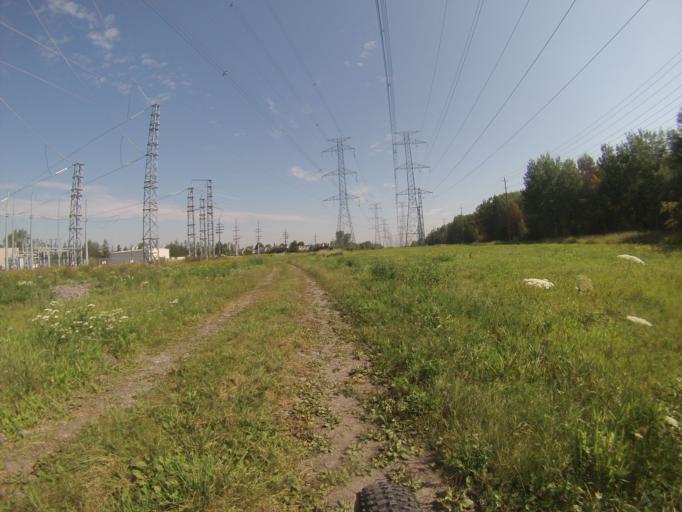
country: CA
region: Ontario
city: Ottawa
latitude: 45.3712
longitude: -75.6459
